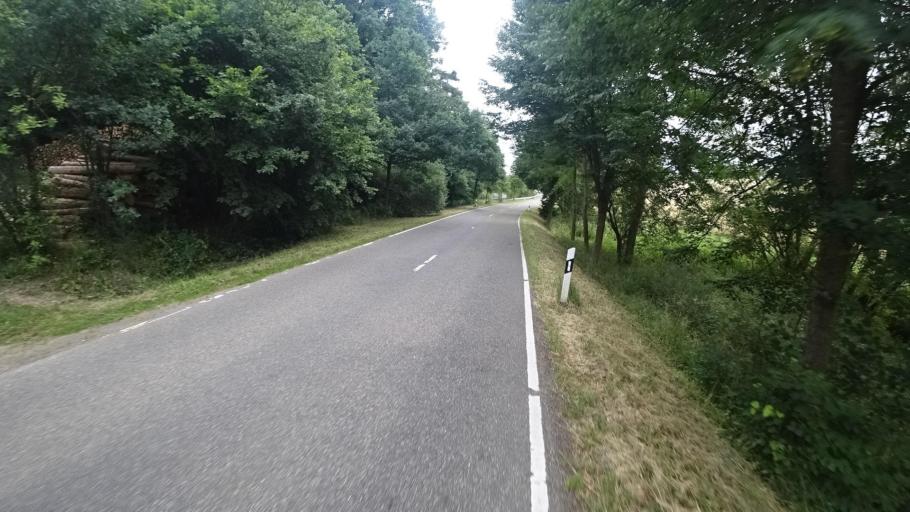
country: DE
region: Rheinland-Pfalz
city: Birnbach
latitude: 50.6986
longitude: 7.5821
